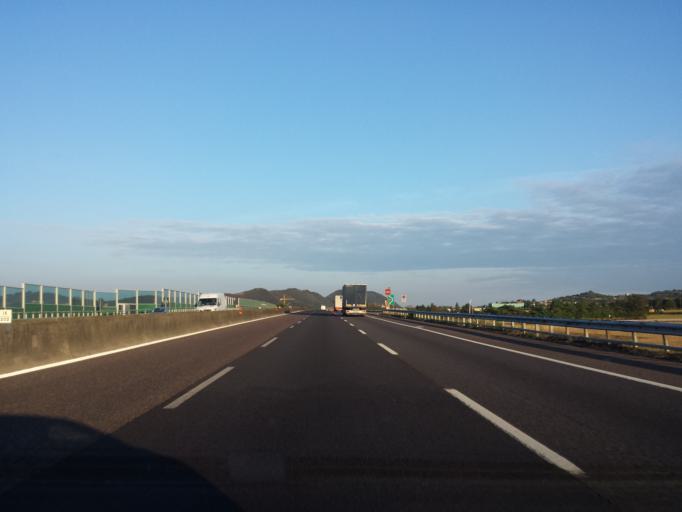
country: IT
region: Lombardy
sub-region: Provincia di Brescia
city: Cazzago San Martino-Calino
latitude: 45.5735
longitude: 10.0262
